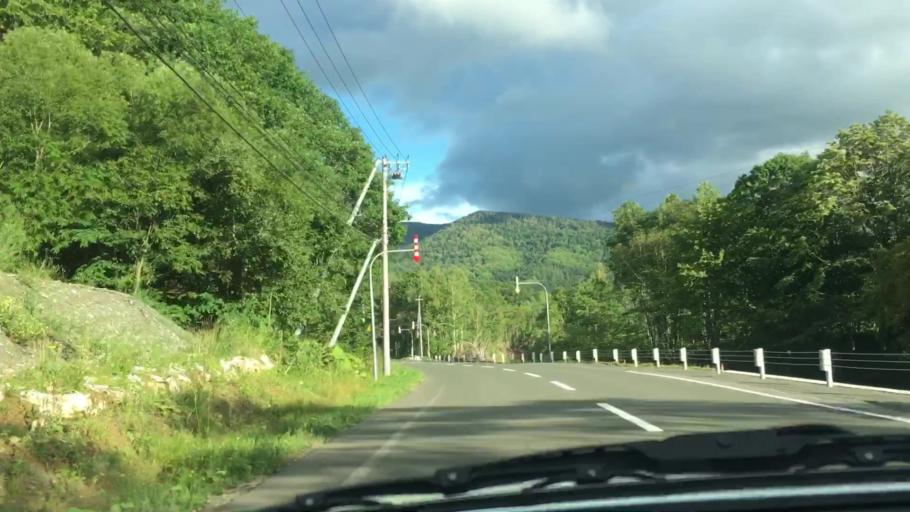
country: JP
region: Hokkaido
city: Shimo-furano
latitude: 43.1145
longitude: 142.6853
